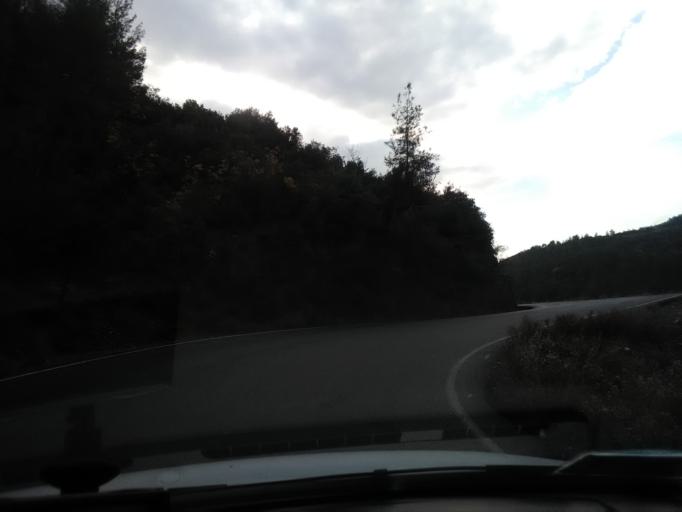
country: TR
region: Antalya
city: Gazipasa
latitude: 36.2951
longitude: 32.3806
